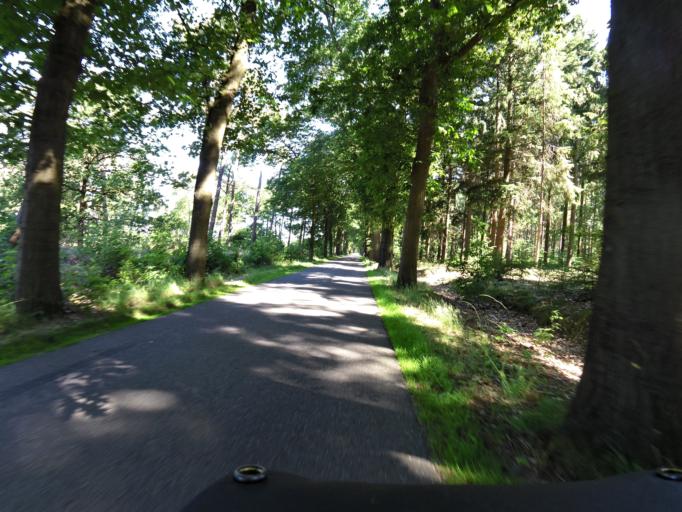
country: NL
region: Overijssel
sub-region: Gemeente Dalfsen
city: Dalfsen
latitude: 52.4900
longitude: 6.3581
